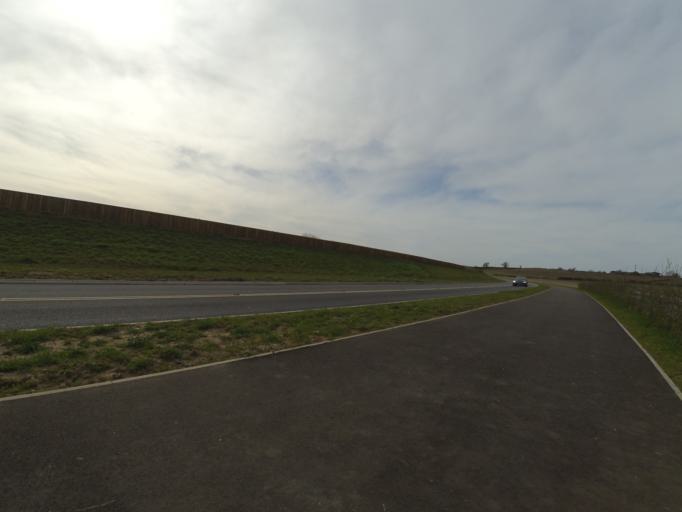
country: GB
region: England
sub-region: Warwickshire
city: Rugby
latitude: 52.3691
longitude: -1.2102
